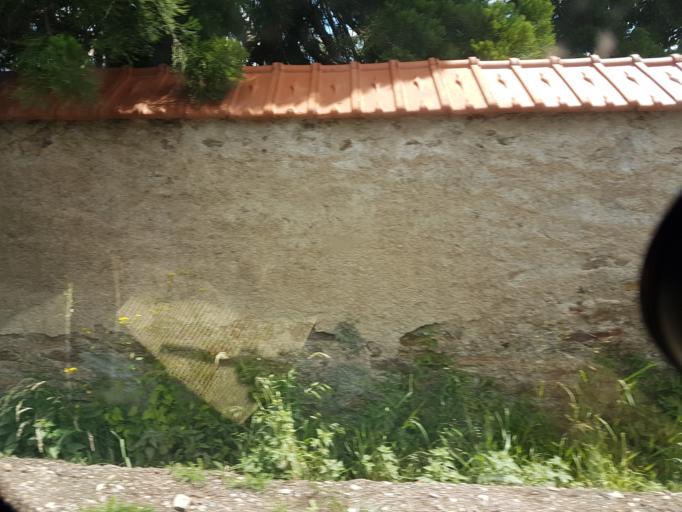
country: FR
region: Bourgogne
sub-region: Departement de Saone-et-Loire
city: Epinac
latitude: 46.9747
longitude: 4.4922
